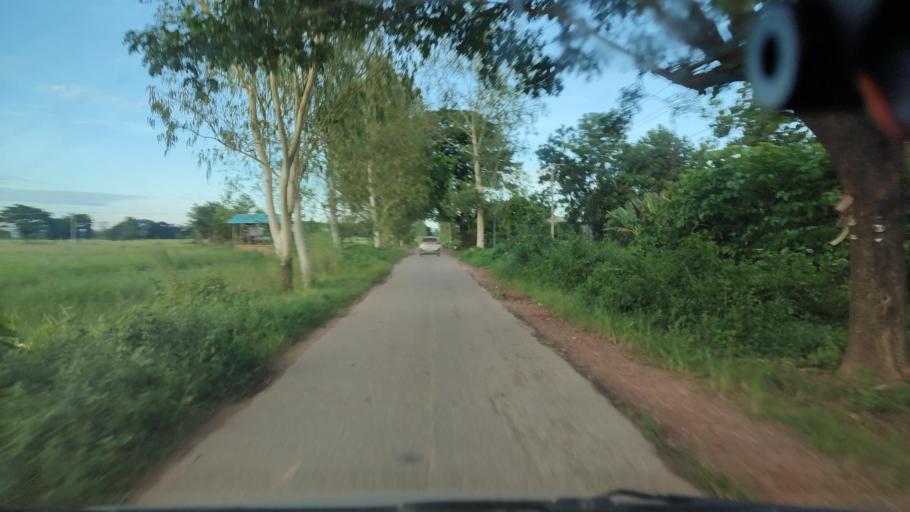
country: MM
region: Bago
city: Tharyarwady
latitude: 17.7120
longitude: 95.8157
